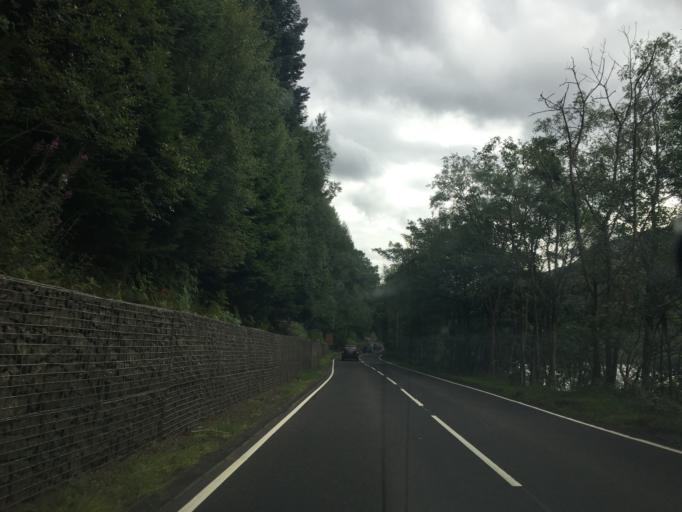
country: GB
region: Scotland
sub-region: Stirling
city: Callander
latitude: 56.3057
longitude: -4.3213
